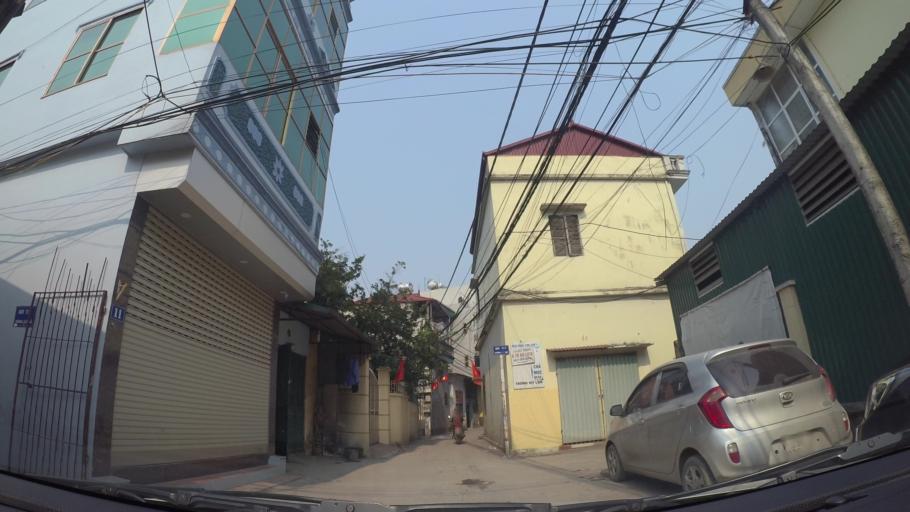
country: VN
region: Ha Noi
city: Ha Dong
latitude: 20.9991
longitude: 105.7521
